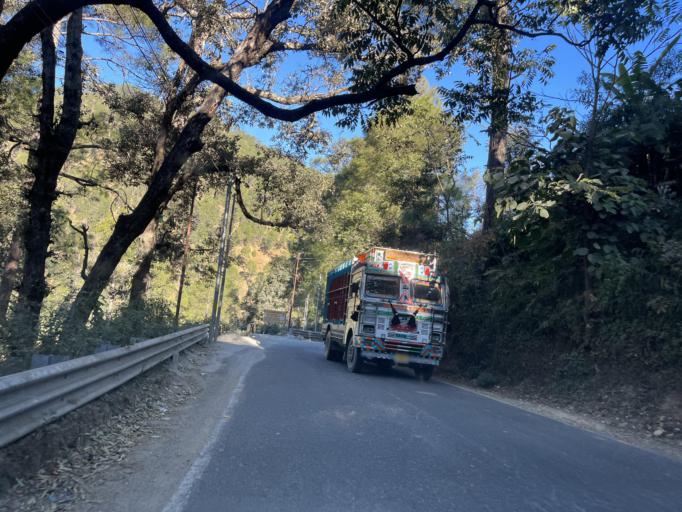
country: IN
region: Uttarakhand
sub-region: Naini Tal
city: Bhowali
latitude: 29.4063
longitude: 79.5148
